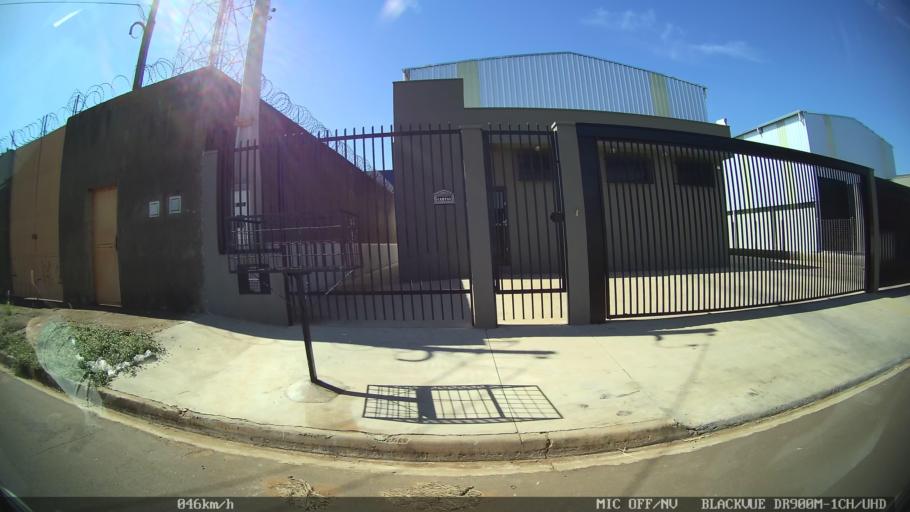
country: BR
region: Sao Paulo
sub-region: Franca
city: Franca
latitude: -20.5435
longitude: -47.4642
